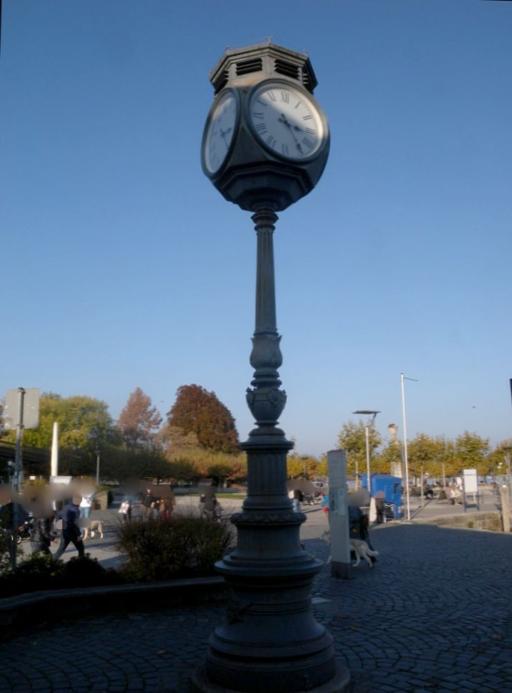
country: DE
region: Baden-Wuerttemberg
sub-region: Freiburg Region
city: Konstanz
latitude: 47.6604
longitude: 9.1785
